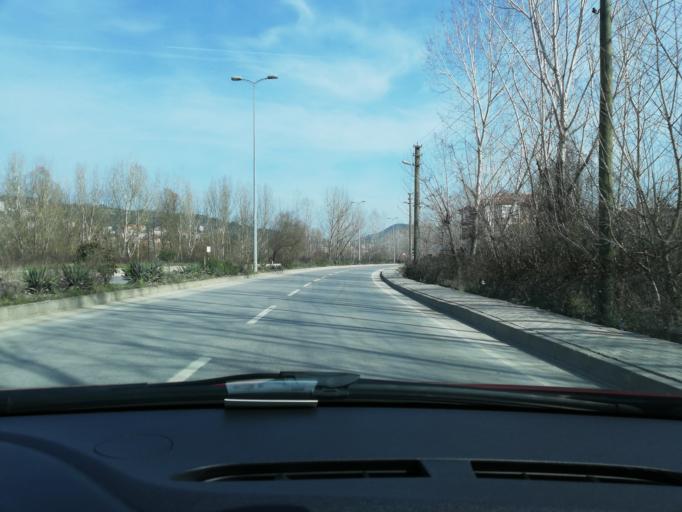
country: TR
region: Bartin
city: Bartin
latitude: 41.6355
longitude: 32.3488
